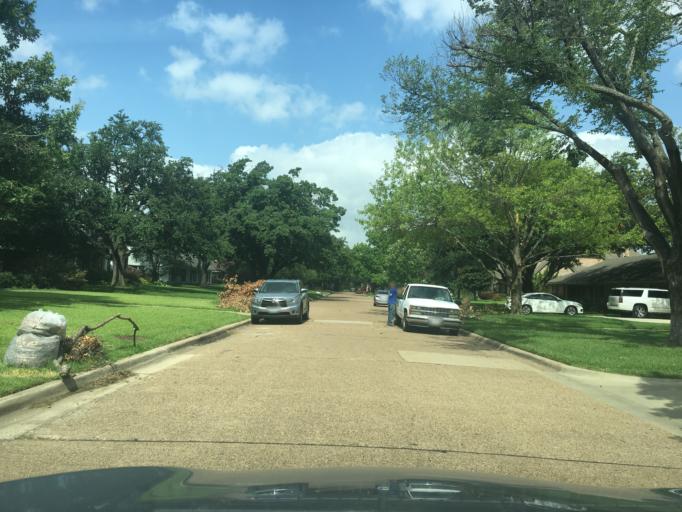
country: US
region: Texas
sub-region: Dallas County
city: Addison
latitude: 32.9121
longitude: -96.8318
